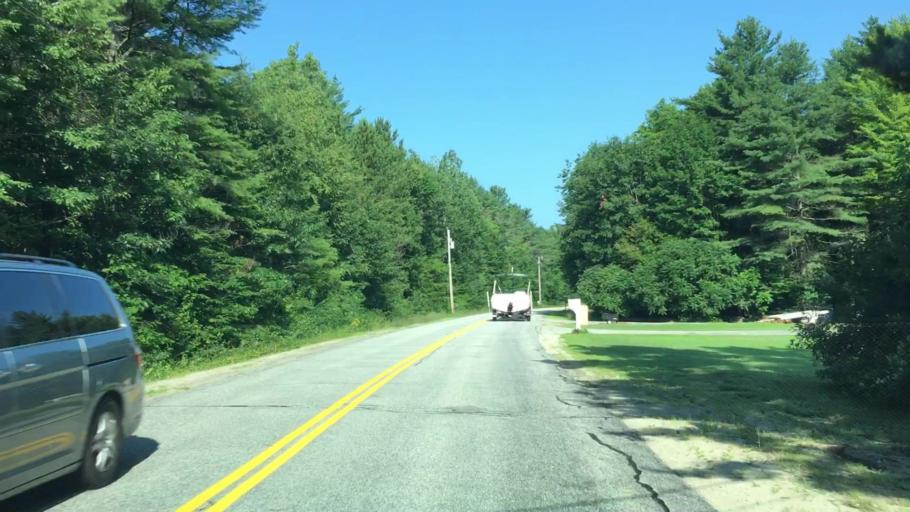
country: US
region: Maine
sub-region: Androscoggin County
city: Poland
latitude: 44.0435
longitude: -70.3551
